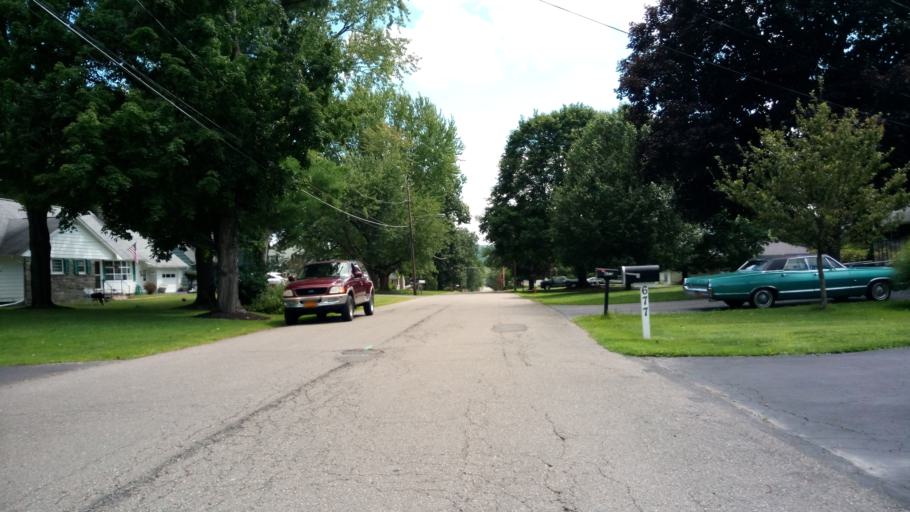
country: US
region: New York
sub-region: Chemung County
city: West Elmira
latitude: 42.0883
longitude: -76.8351
